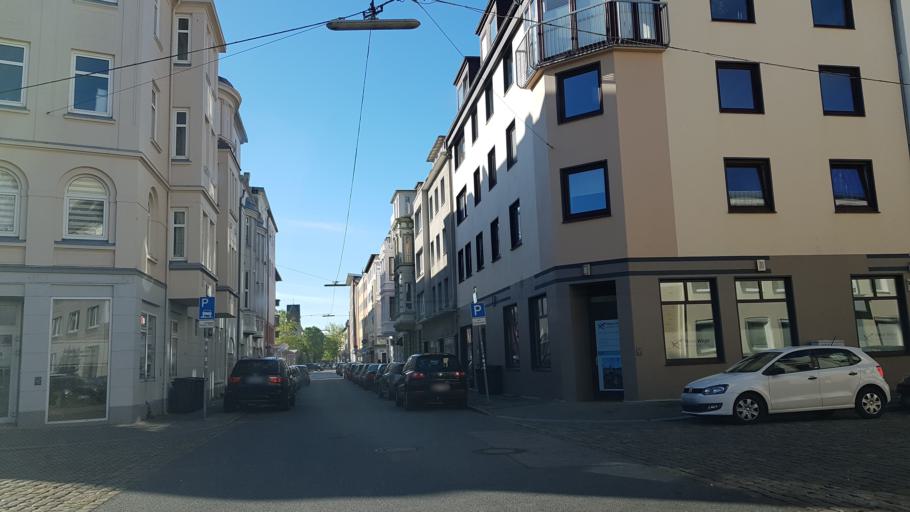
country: DE
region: Bremen
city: Bremerhaven
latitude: 53.5492
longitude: 8.5750
